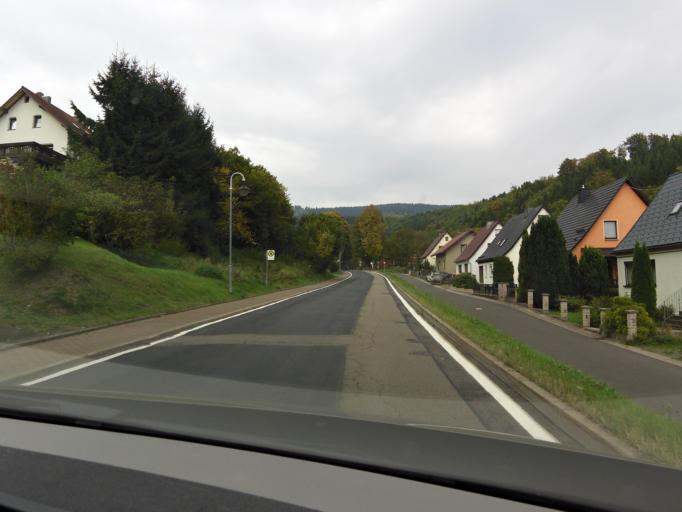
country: DE
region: Thuringia
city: Pappenheim
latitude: 50.8017
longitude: 10.4701
